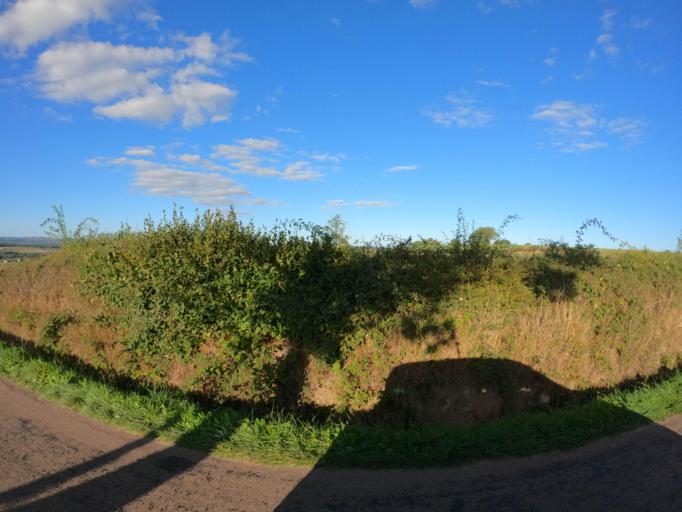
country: FR
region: Bourgogne
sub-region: Departement de Saone-et-Loire
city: Ecuisses
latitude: 46.7479
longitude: 4.5341
